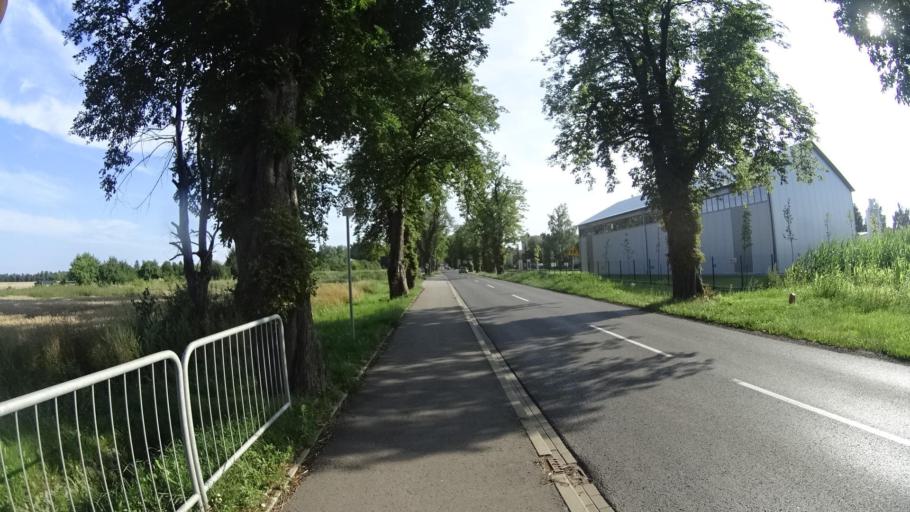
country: PL
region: Masovian Voivodeship
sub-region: Powiat pruszkowski
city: Nadarzyn
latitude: 52.0536
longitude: 20.7845
